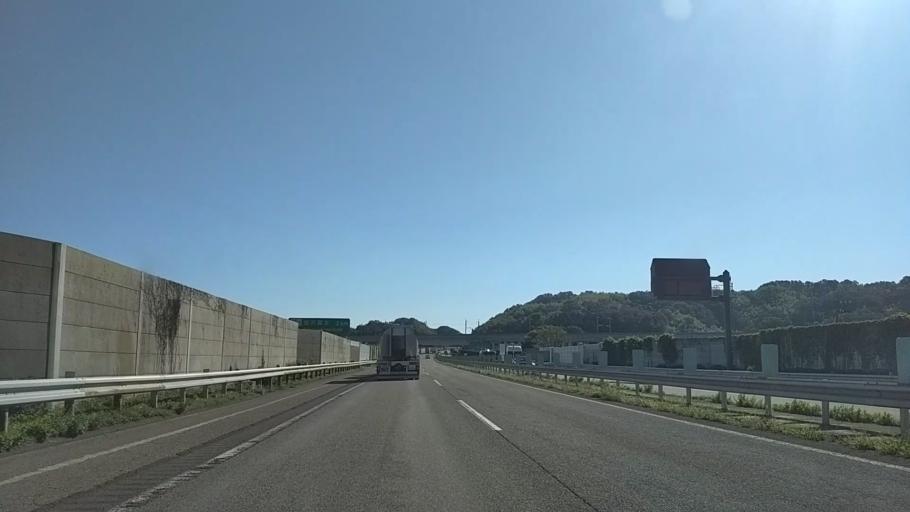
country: JP
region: Ishikawa
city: Kanazawa-shi
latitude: 36.6084
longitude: 136.6810
